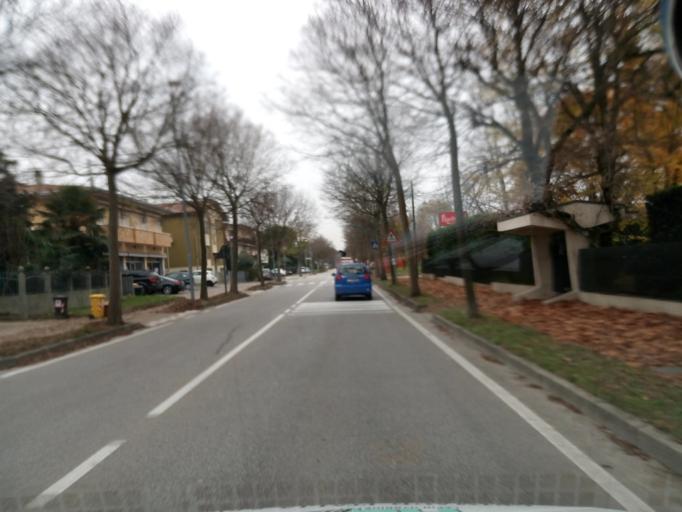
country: IT
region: Veneto
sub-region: Provincia di Padova
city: Vigonza
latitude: 45.4375
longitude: 11.9606
